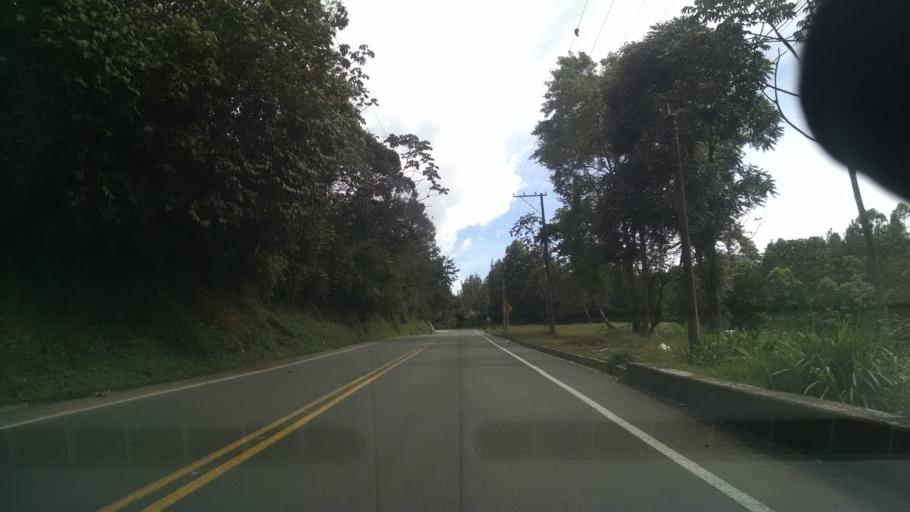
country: CO
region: Antioquia
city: Caldas
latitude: 6.0436
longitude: -75.6294
